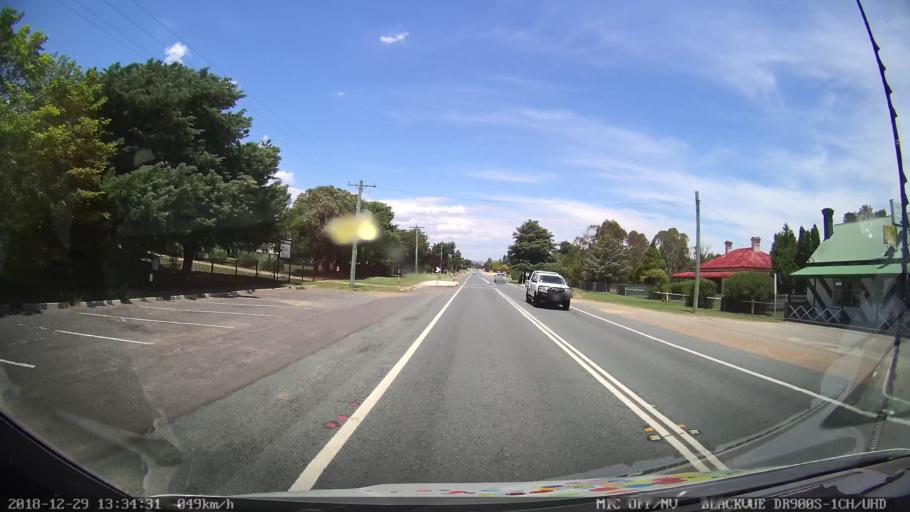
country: AU
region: New South Wales
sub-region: Cooma-Monaro
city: Cooma
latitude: -35.9537
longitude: 149.1468
